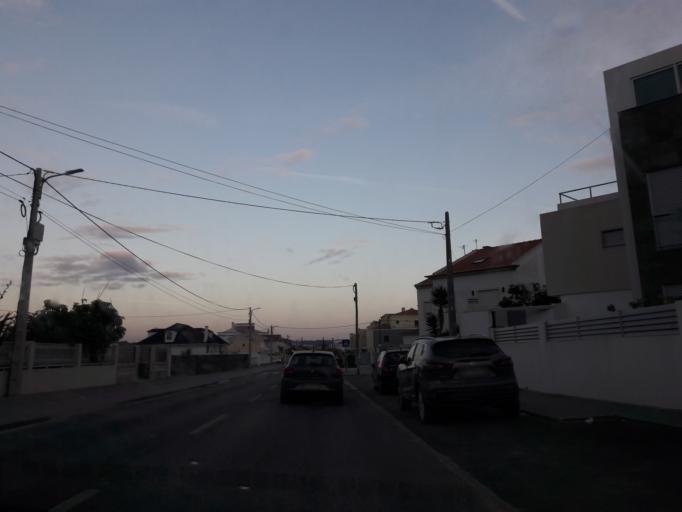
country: PT
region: Leiria
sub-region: Peniche
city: Atouguia da Baleia
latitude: 39.3697
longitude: -9.3274
